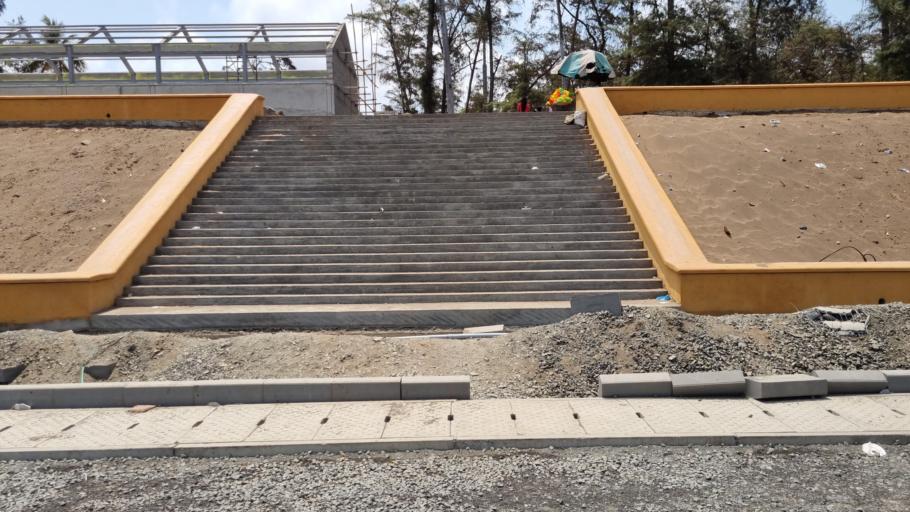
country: IN
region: Daman and Diu
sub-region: Daman District
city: Daman
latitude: 20.4426
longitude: 72.8316
